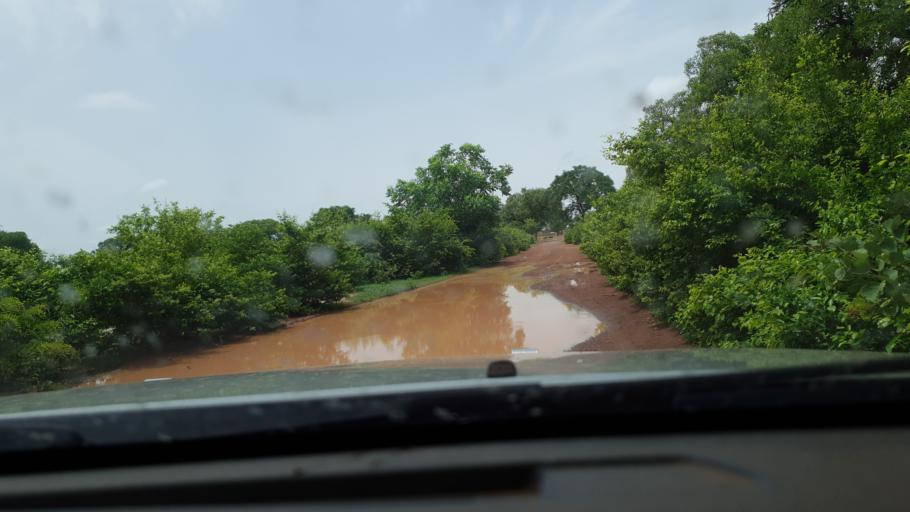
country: ML
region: Koulikoro
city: Dioila
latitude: 12.5220
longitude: -6.8122
